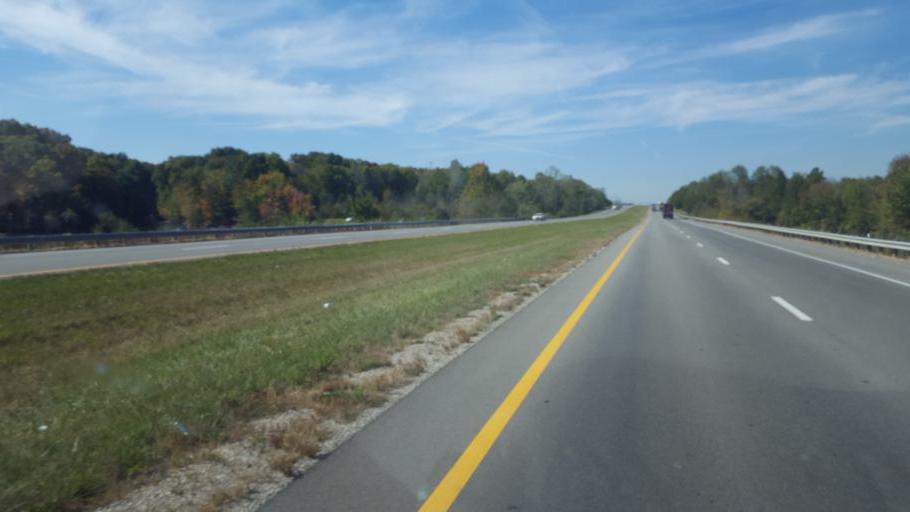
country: US
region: Ohio
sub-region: Delaware County
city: Lewis Center
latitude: 40.2695
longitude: -82.9529
